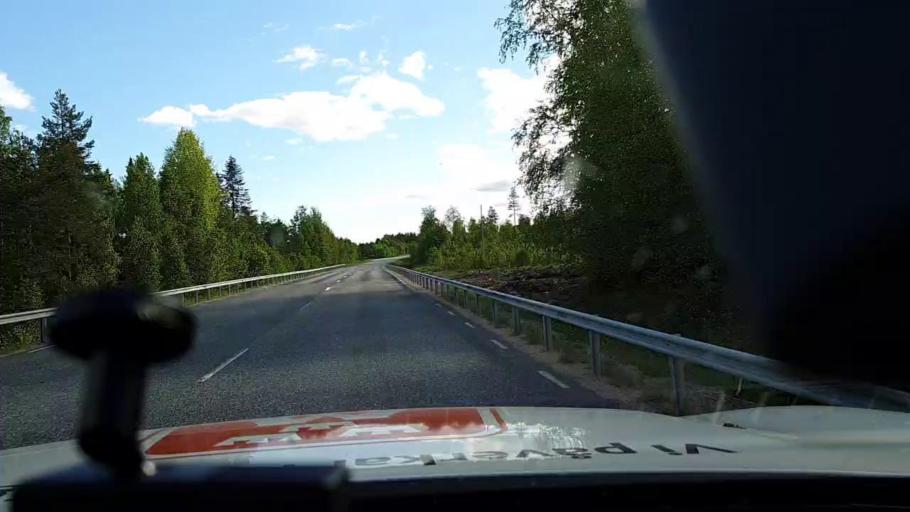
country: FI
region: Lapland
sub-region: Torniolaakso
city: Ylitornio
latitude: 66.3386
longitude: 23.6449
